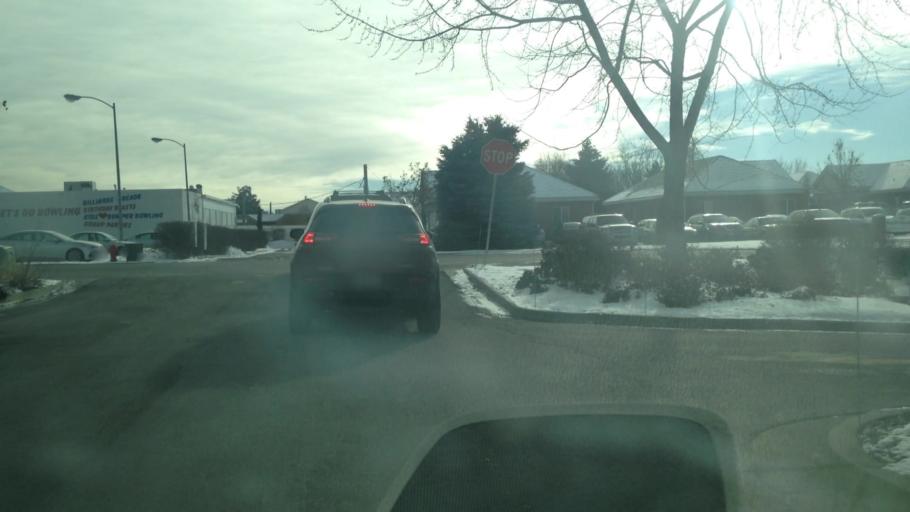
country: US
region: Utah
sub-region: Cache County
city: Logan
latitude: 41.7547
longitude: -111.8357
